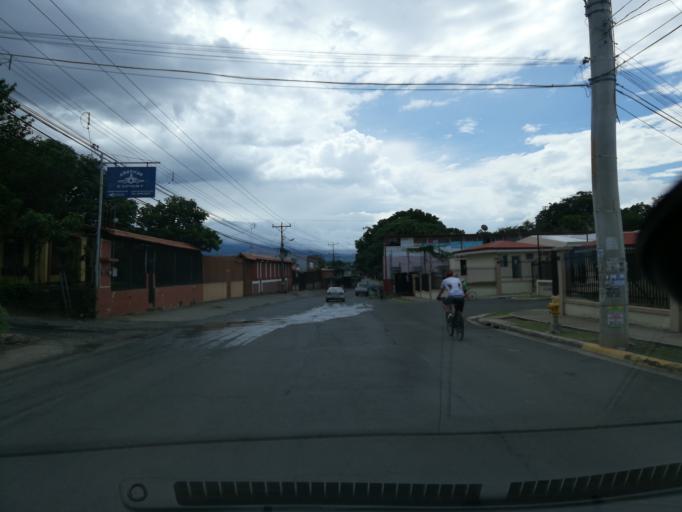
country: CR
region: Alajuela
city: Alajuela
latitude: 9.9926
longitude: -84.2344
